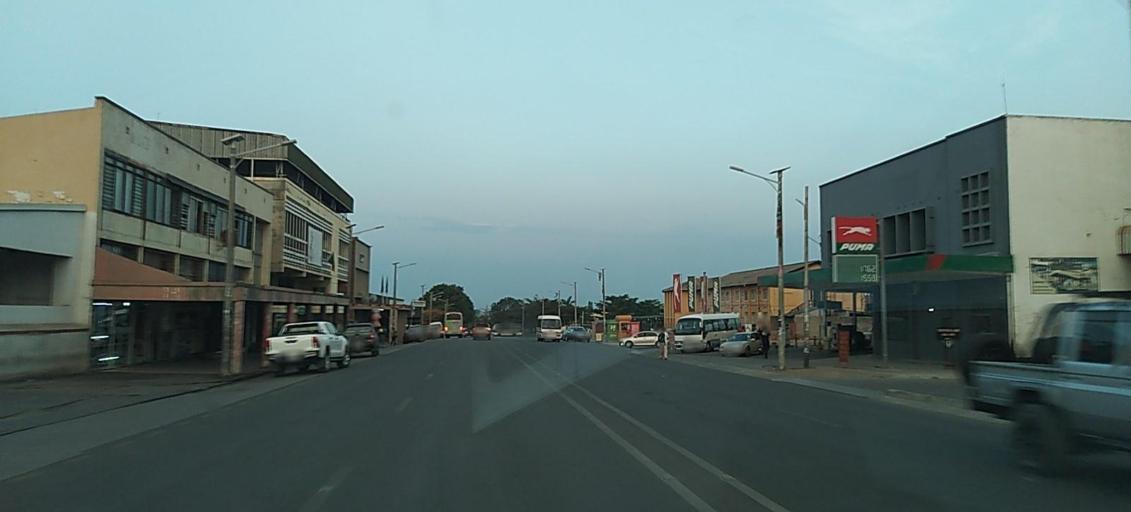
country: ZM
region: Copperbelt
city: Chingola
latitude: -12.5454
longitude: 27.8648
